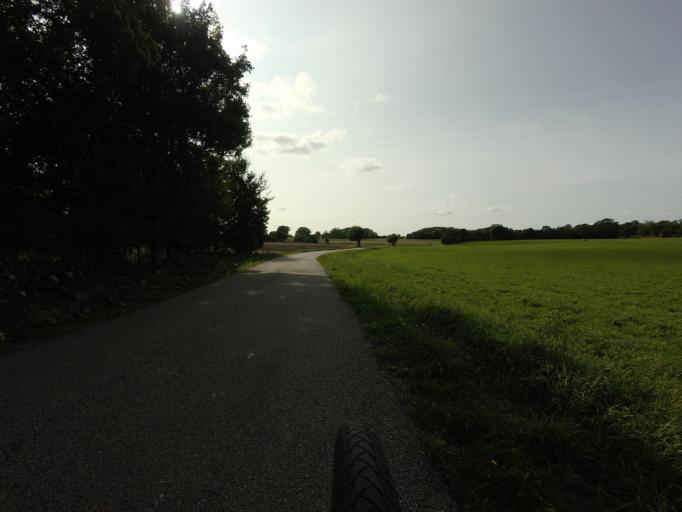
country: DK
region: Zealand
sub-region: Faxe Kommune
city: Fakse
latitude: 55.2069
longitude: 12.1174
